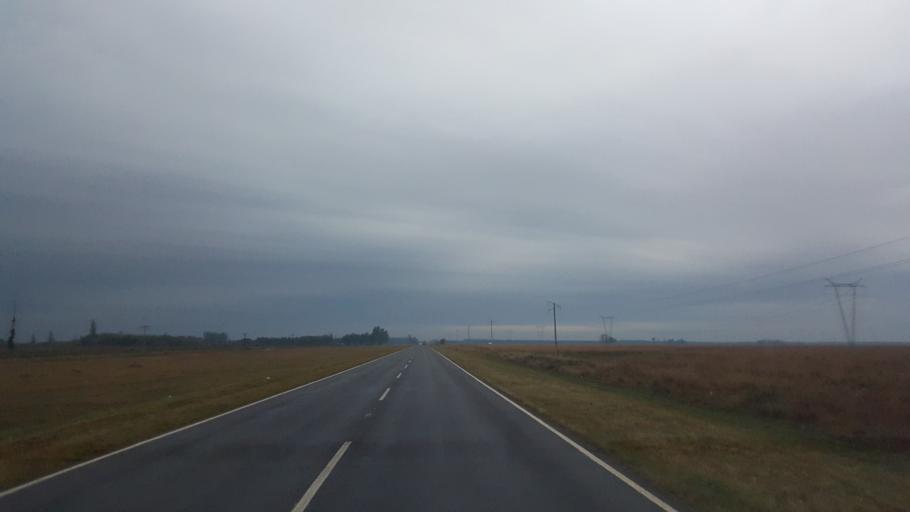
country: AR
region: Corrientes
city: Ituzaingo
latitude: -27.5925
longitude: -56.4746
